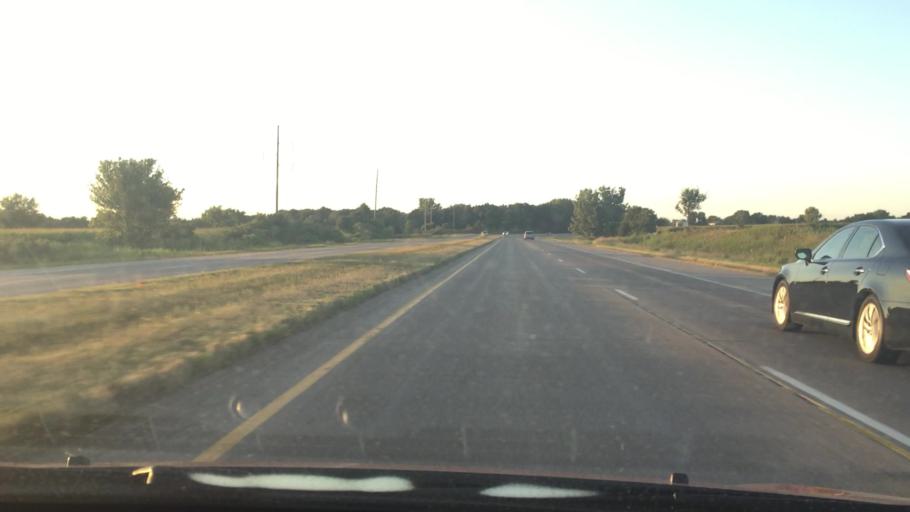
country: US
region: Iowa
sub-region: Muscatine County
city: Muscatine
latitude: 41.4419
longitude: -91.0921
